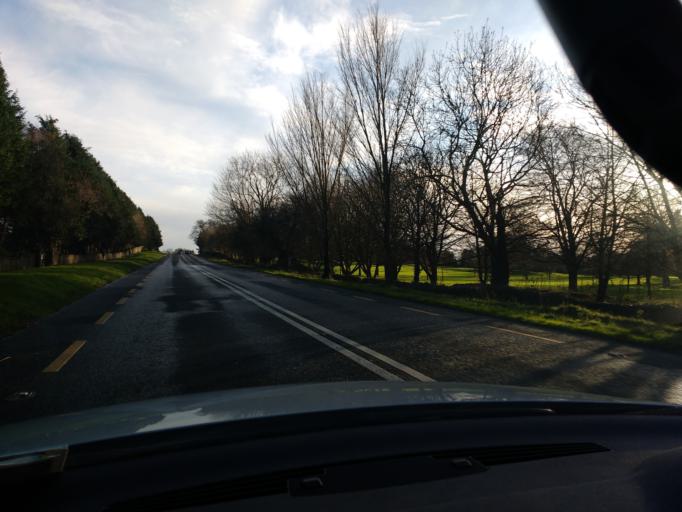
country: IE
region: Munster
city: Thurles
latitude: 52.6600
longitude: -7.8023
